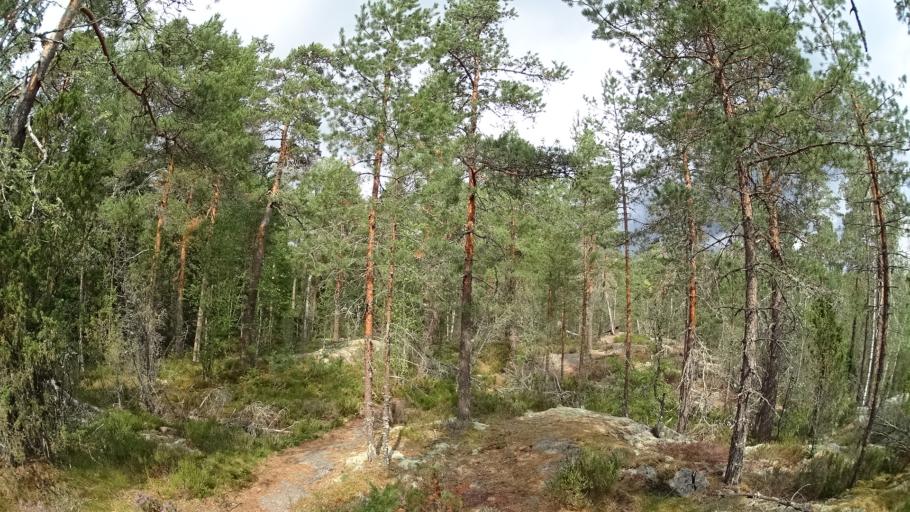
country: FI
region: Uusimaa
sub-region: Helsinki
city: Espoo
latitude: 60.3031
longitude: 24.5817
